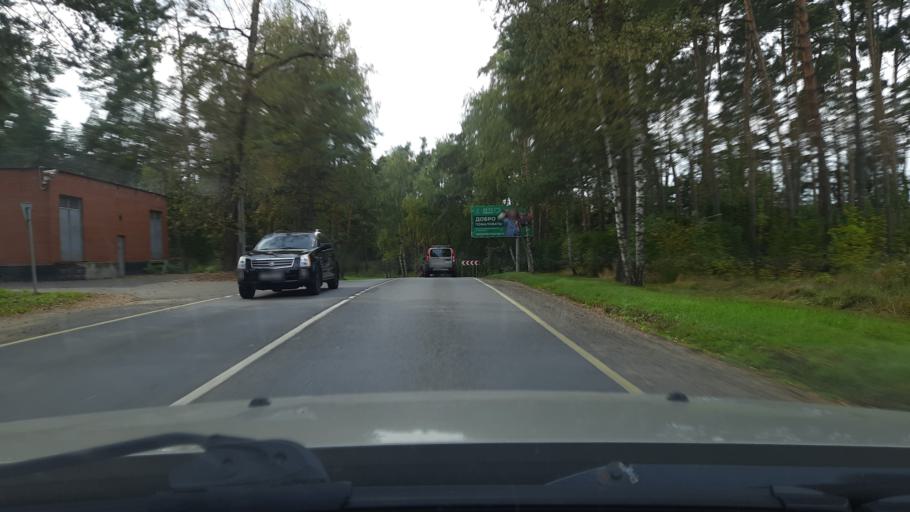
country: RU
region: Moskovskaya
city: Petrovo-Dal'neye
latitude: 55.7505
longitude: 37.2097
